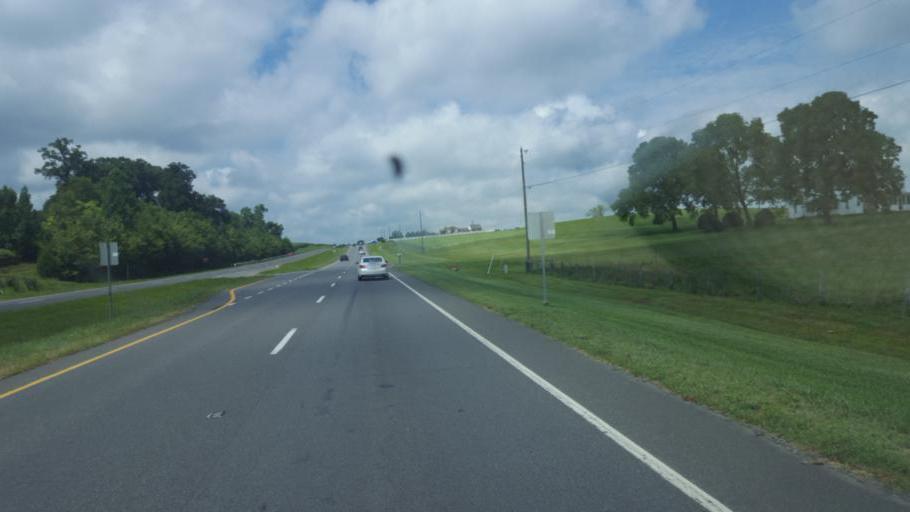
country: US
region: Virginia
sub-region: Fauquier County
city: Bealeton
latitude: 38.4336
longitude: -77.6345
